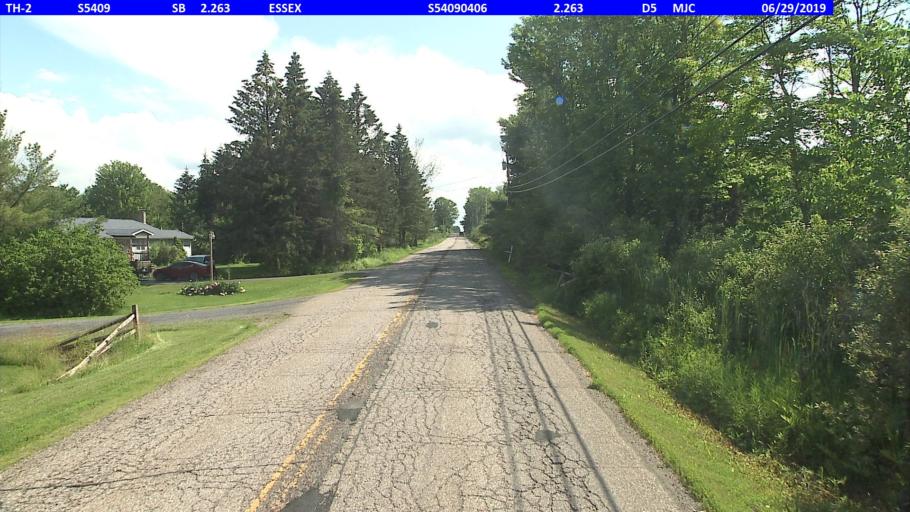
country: US
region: Vermont
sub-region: Chittenden County
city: Essex Junction
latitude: 44.5410
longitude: -73.0734
